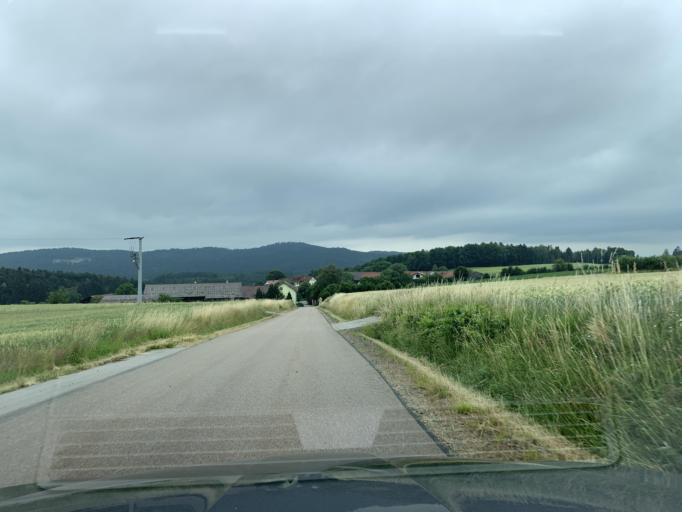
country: DE
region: Bavaria
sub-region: Upper Palatinate
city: Thanstein
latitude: 49.4110
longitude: 12.4499
